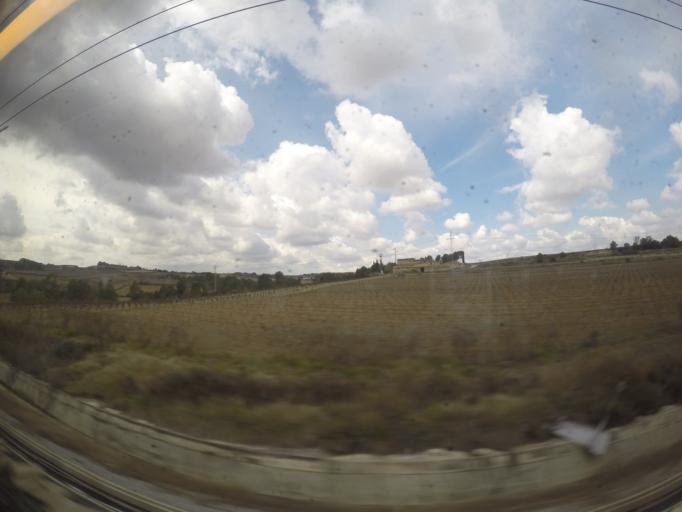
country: ES
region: Catalonia
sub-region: Provincia de Barcelona
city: Sant Llorenc d'Hortons
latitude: 41.4421
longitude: 1.8316
